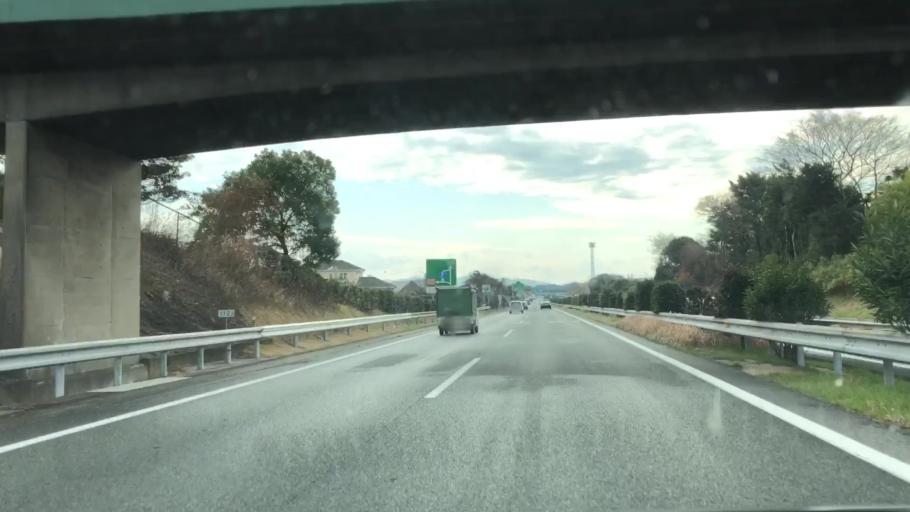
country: JP
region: Fukuoka
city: Kurume
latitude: 33.2645
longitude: 130.5387
